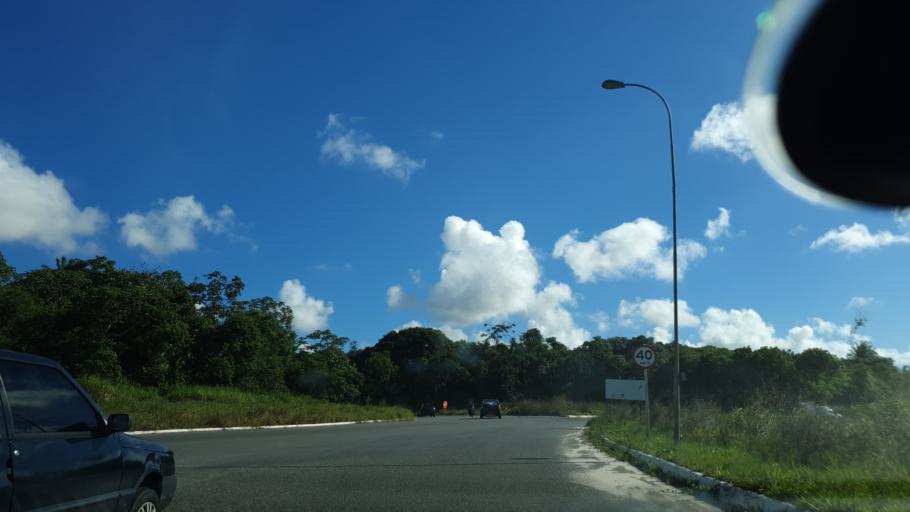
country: BR
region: Bahia
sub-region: Camacari
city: Camacari
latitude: -12.6794
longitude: -38.2833
